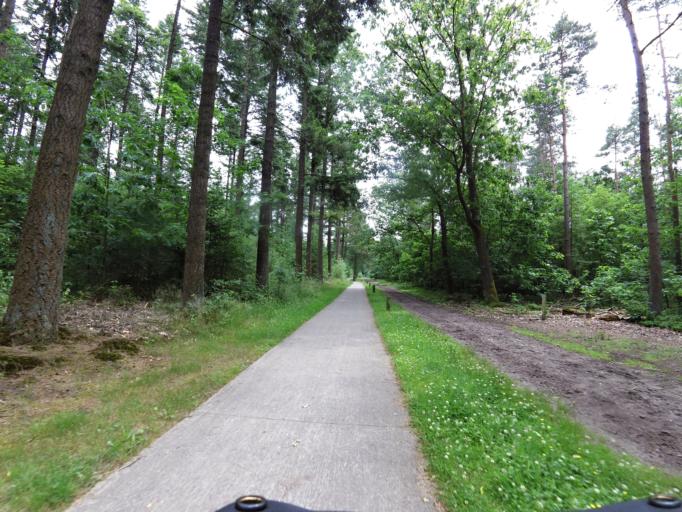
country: NL
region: Gelderland
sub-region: Gemeente Apeldoorn
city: Loenen
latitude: 52.1422
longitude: 6.0172
